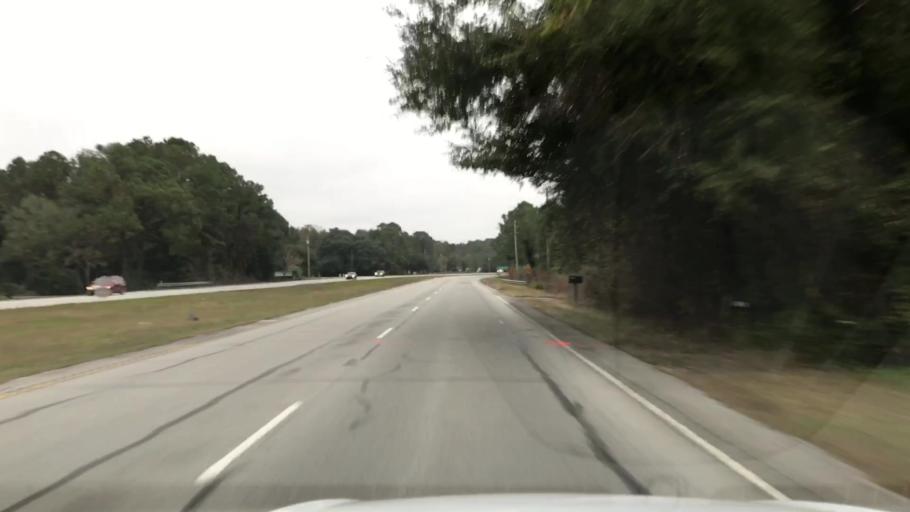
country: US
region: South Carolina
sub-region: Charleston County
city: Awendaw
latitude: 33.0757
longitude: -79.5113
